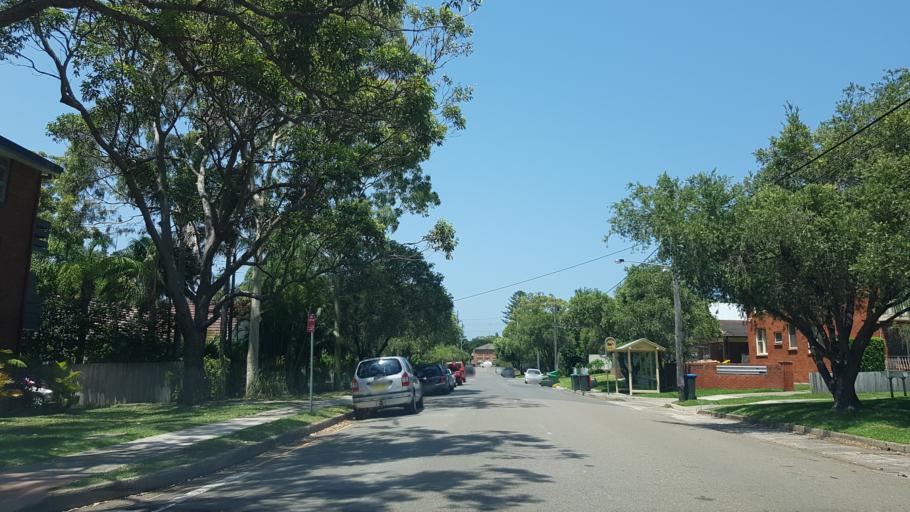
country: AU
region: New South Wales
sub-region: Pittwater
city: Newport
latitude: -33.6583
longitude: 151.3144
